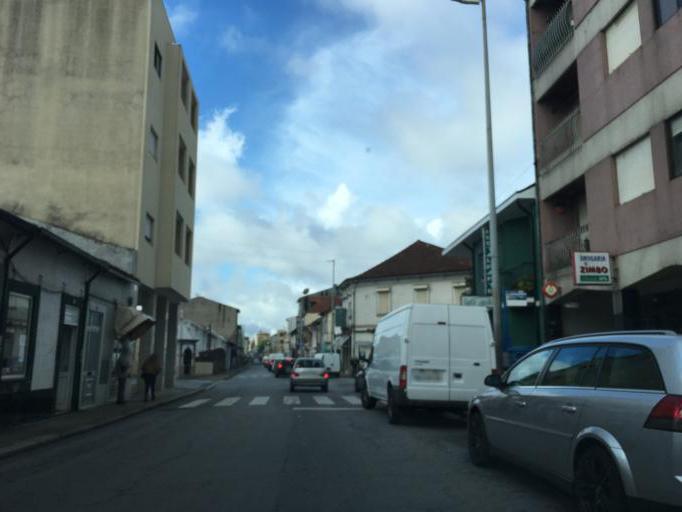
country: PT
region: Porto
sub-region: Matosinhos
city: Sao Mamede de Infesta
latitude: 41.1864
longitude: -8.6130
